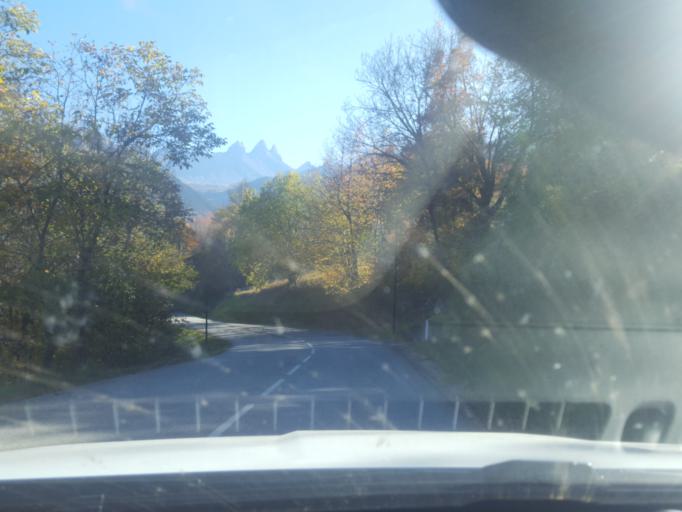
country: FR
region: Rhone-Alpes
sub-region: Departement de la Savoie
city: Saint-Jean-de-Maurienne
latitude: 45.2442
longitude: 6.3101
